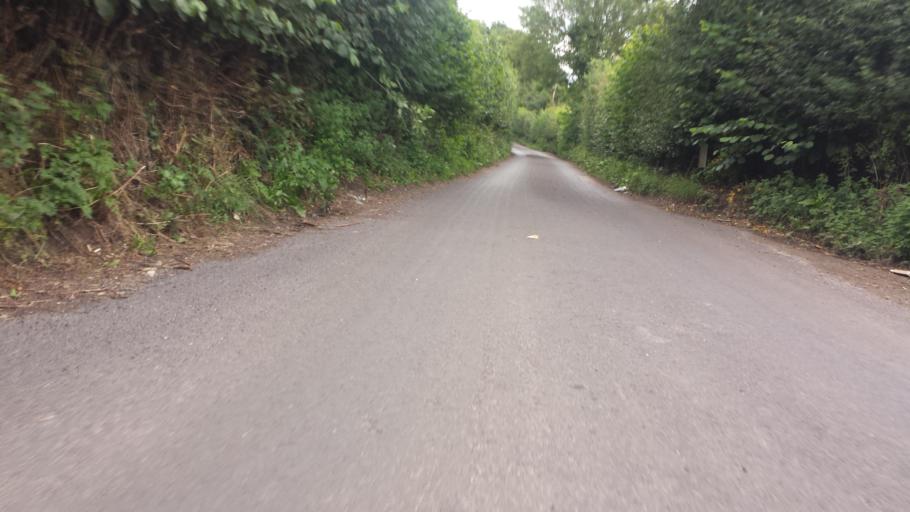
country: GB
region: England
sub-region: Kent
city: Swanley
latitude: 51.3710
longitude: 0.1559
